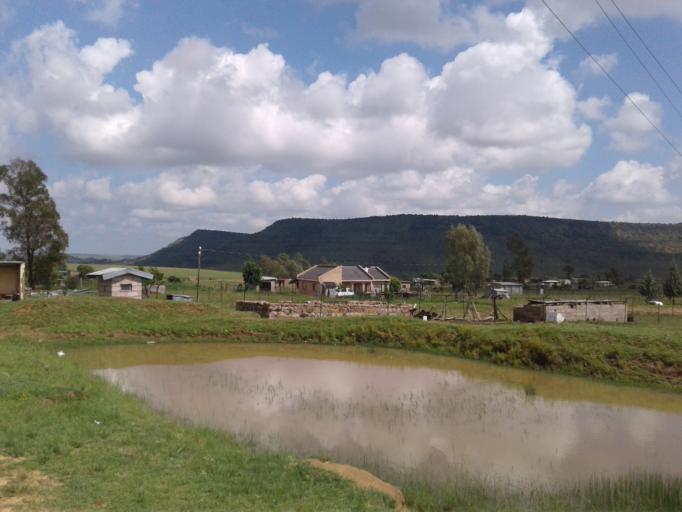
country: LS
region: Mafeteng
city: Mafeteng
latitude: -29.7536
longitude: 27.1115
